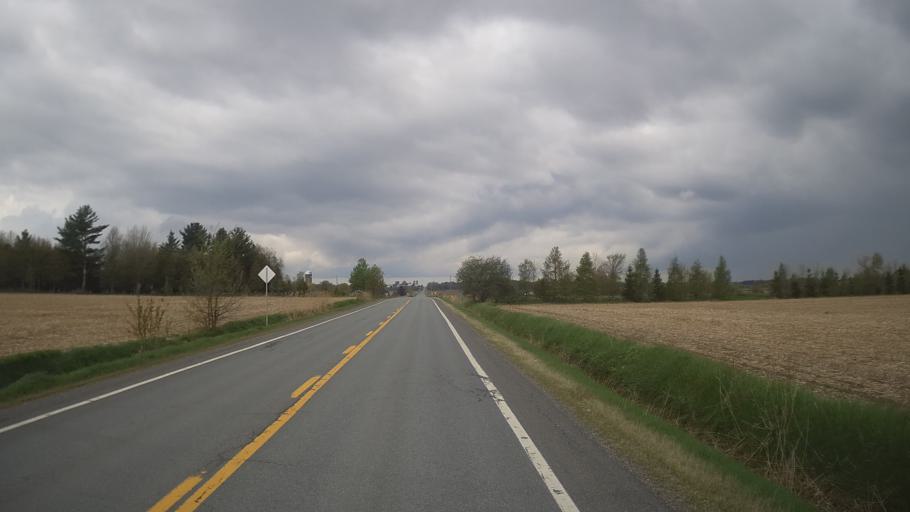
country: CA
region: Quebec
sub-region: Monteregie
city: Farnham
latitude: 45.2550
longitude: -72.9117
